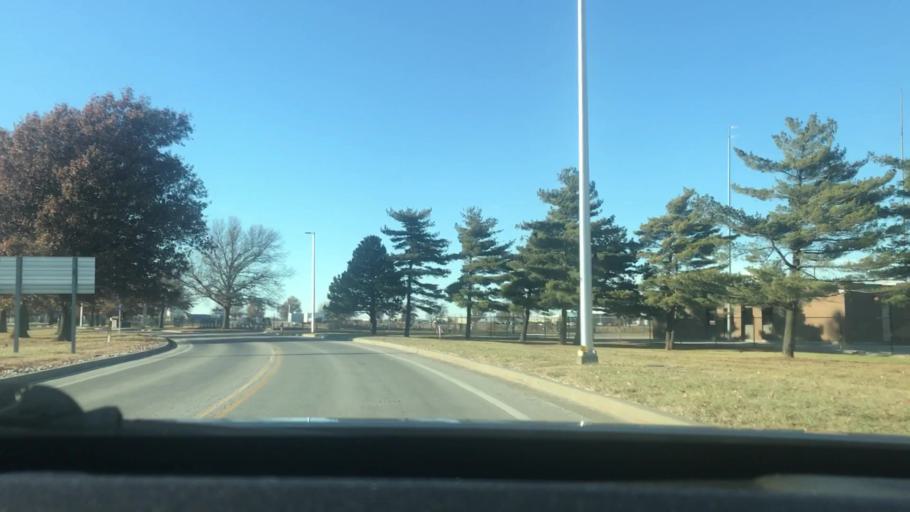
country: US
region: Missouri
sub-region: Platte County
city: Weatherby Lake
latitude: 39.3117
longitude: -94.7112
